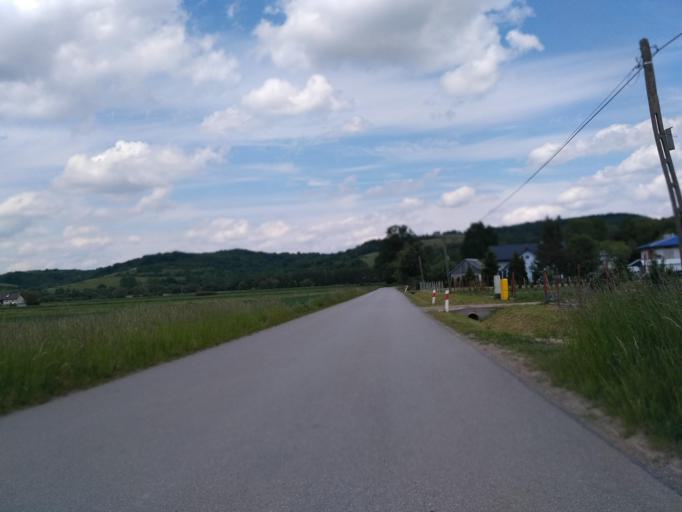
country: PL
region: Subcarpathian Voivodeship
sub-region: Powiat krosnienski
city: Chorkowka
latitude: 49.6037
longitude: 21.6221
